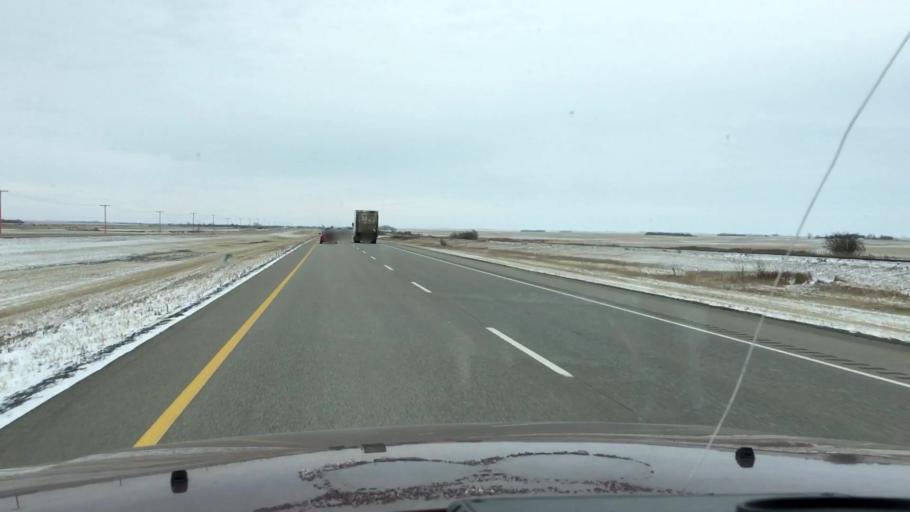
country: CA
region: Saskatchewan
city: Watrous
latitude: 51.1871
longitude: -105.9451
